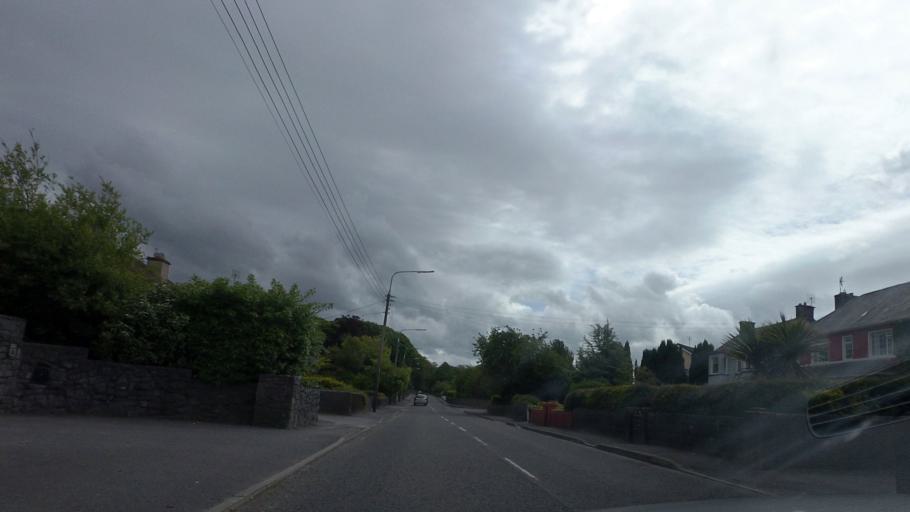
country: IE
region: Munster
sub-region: An Clar
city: Ennis
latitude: 52.8493
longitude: -8.9936
